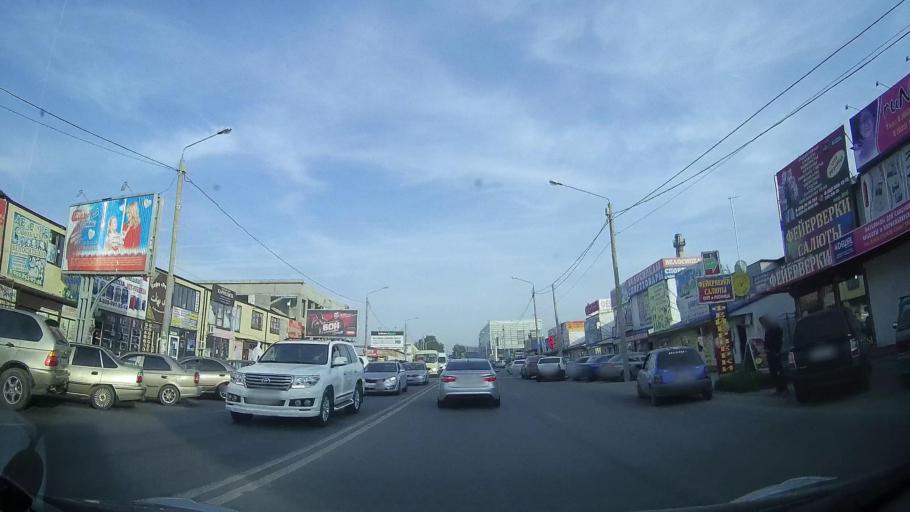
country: RU
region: Rostov
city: Aksay
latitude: 47.2742
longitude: 39.8184
